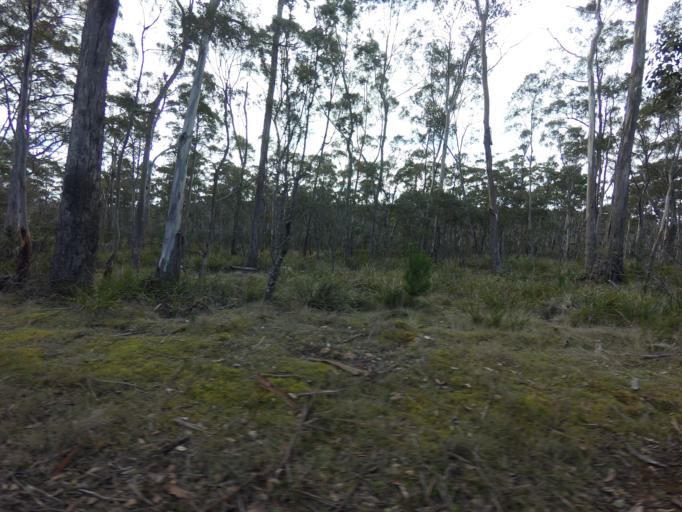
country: AU
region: Tasmania
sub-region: Derwent Valley
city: New Norfolk
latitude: -42.7581
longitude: 146.8849
